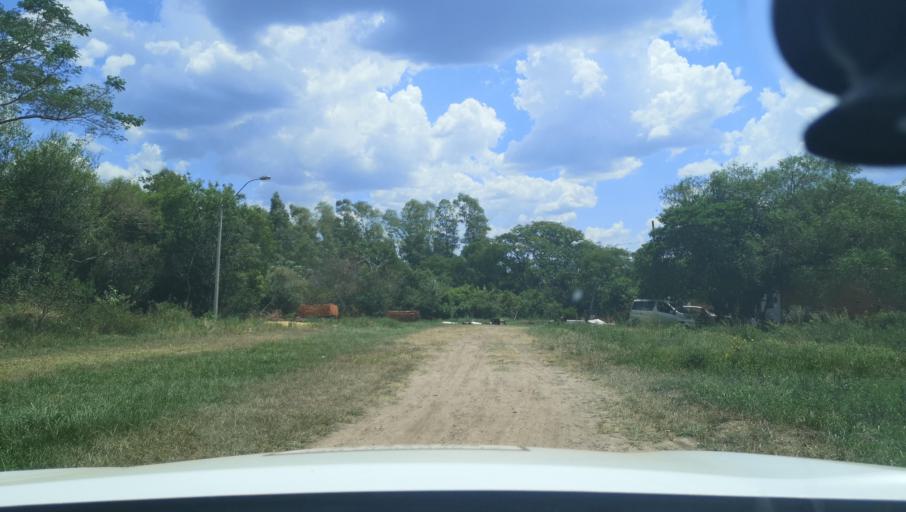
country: PY
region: Itapua
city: Carmen del Parana
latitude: -27.1721
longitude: -56.2414
